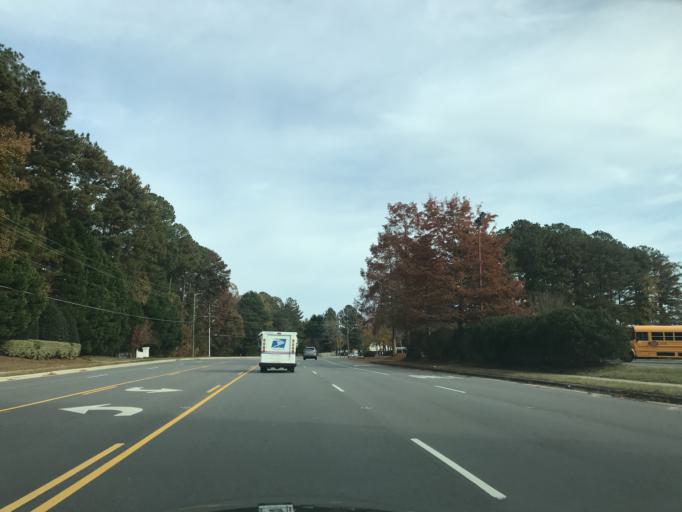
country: US
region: North Carolina
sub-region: Wake County
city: West Raleigh
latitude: 35.8941
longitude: -78.6308
